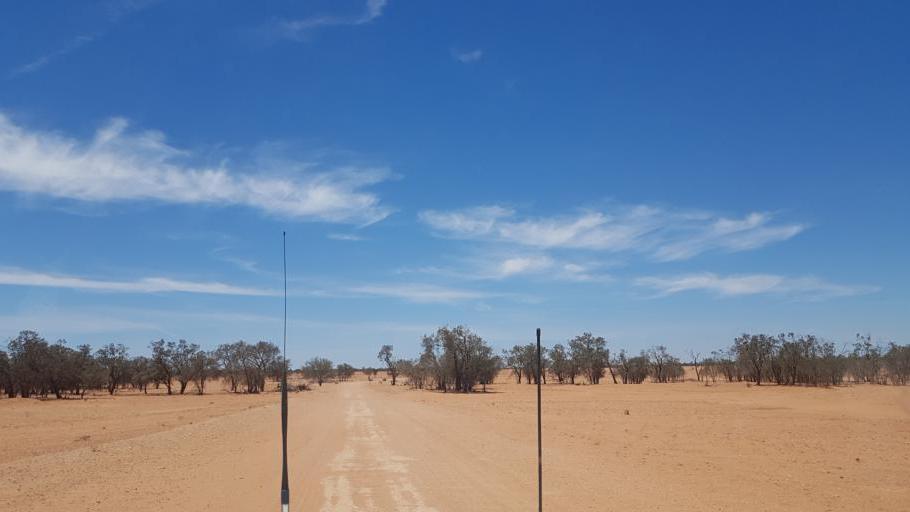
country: AU
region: New South Wales
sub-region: Wentworth
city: Dareton
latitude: -33.3471
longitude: 141.4618
